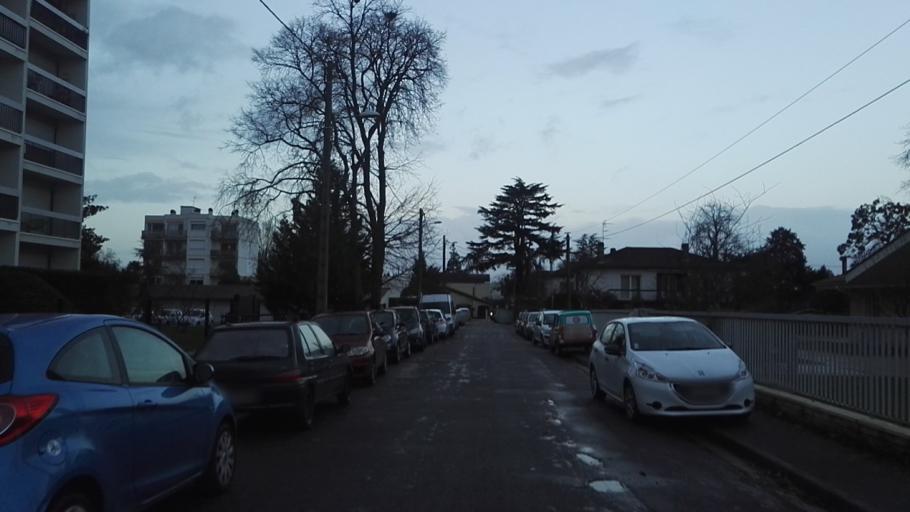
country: FR
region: Aquitaine
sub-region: Departement de la Gironde
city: Talence
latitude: 44.8044
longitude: -0.5847
